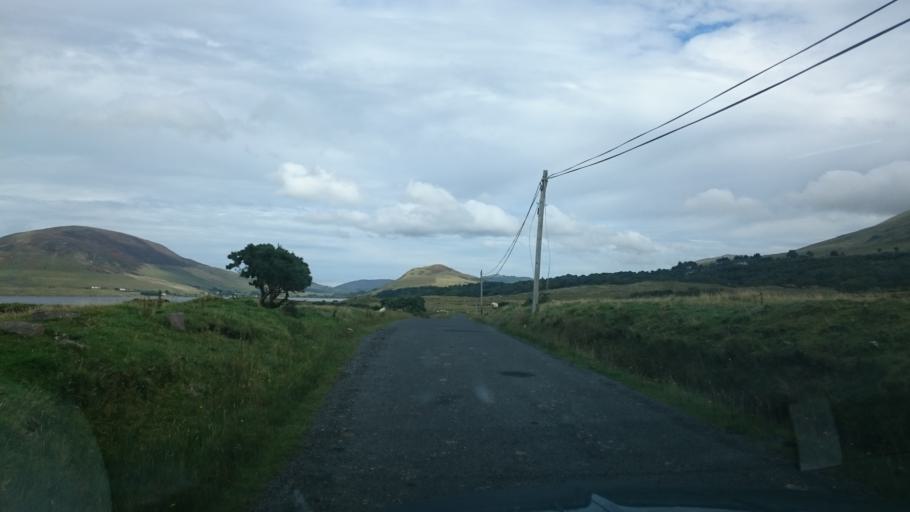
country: IE
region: Connaught
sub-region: Maigh Eo
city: Westport
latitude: 53.9373
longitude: -9.5681
